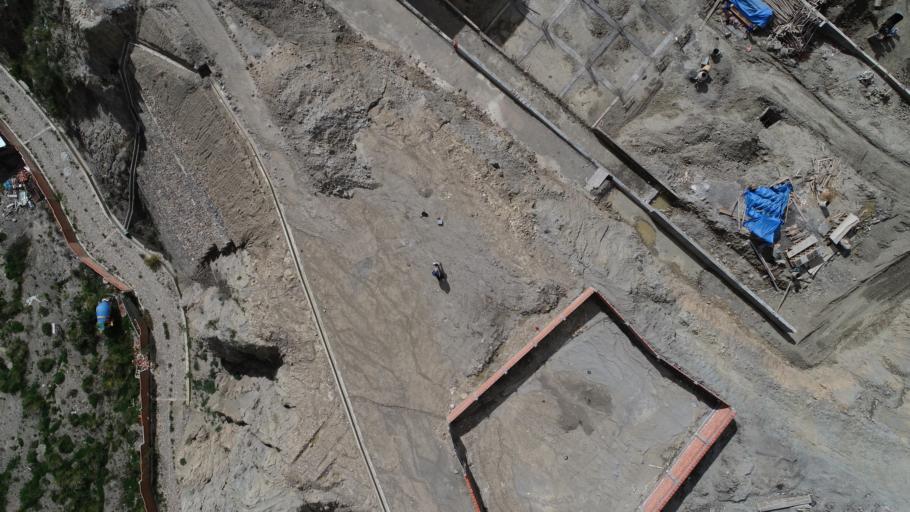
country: BO
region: La Paz
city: La Paz
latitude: -16.5034
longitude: -68.0755
